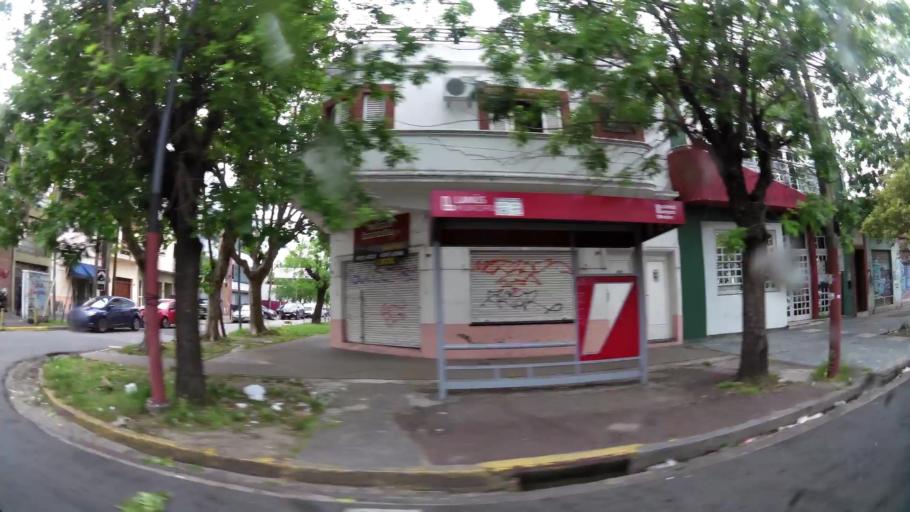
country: AR
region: Buenos Aires
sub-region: Partido de Lanus
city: Lanus
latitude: -34.6923
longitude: -58.3991
